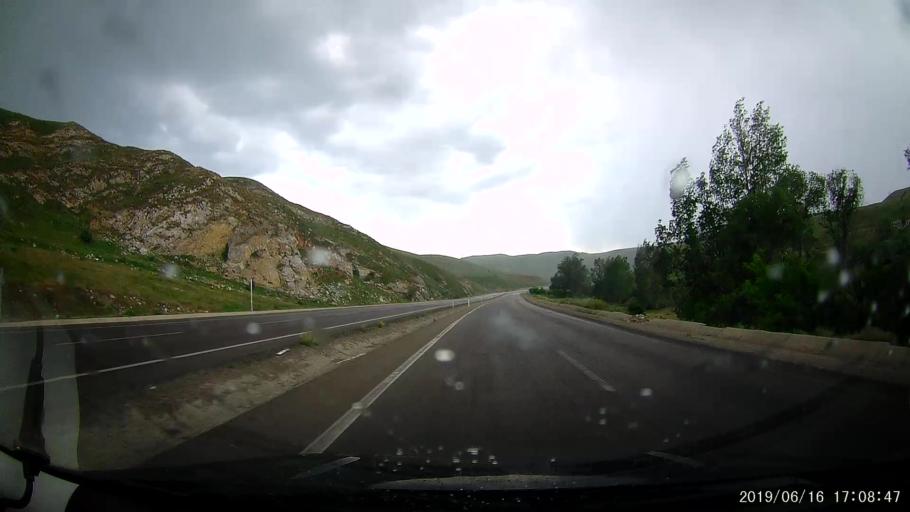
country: TR
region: Erzurum
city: Askale
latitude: 39.9034
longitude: 40.6580
